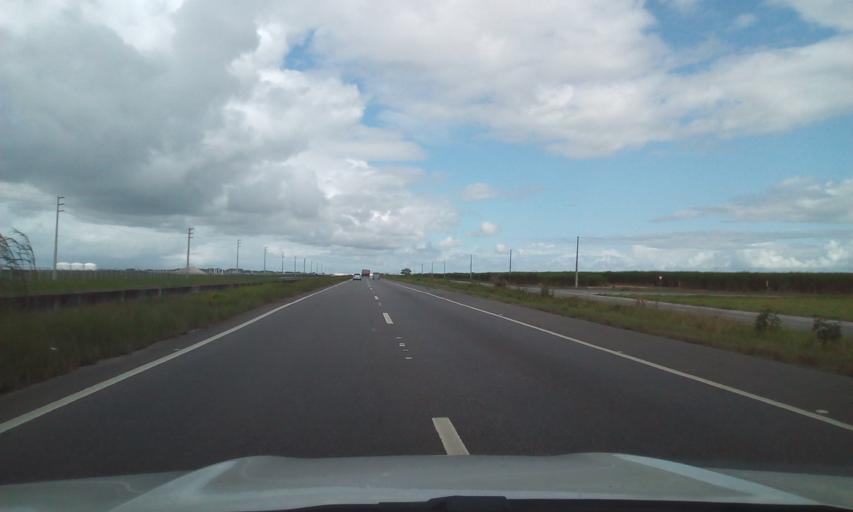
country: BR
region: Pernambuco
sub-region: Goiana
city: Goiana
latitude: -7.6141
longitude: -34.9733
